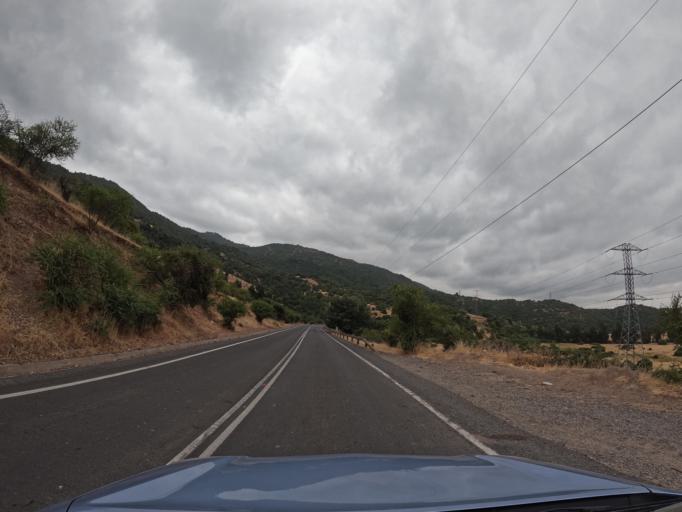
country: CL
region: O'Higgins
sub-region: Provincia de Colchagua
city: Chimbarongo
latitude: -34.7329
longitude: -71.1081
